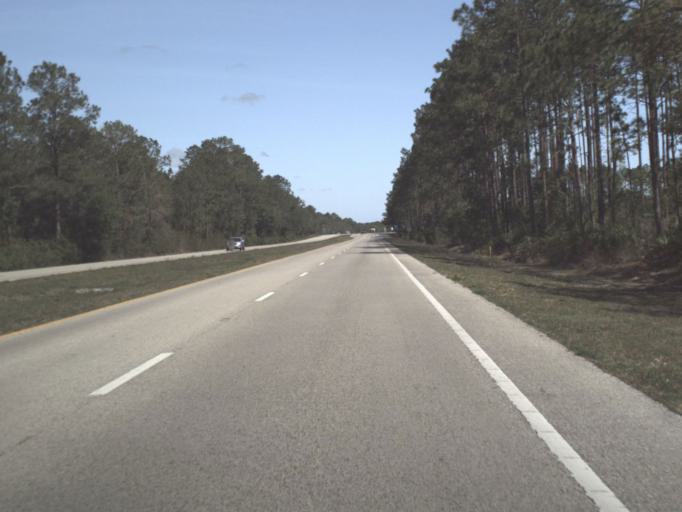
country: US
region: Florida
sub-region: Flagler County
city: Palm Coast
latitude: 29.6362
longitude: -81.2845
